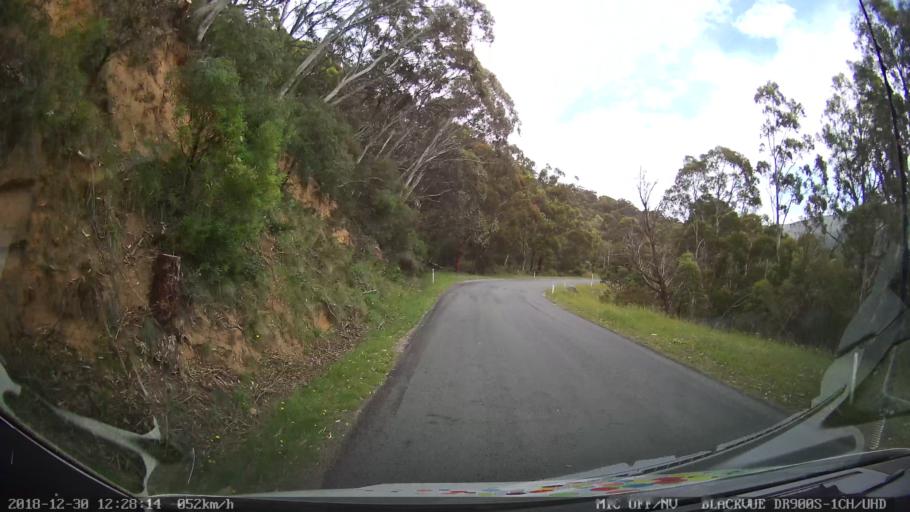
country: AU
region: New South Wales
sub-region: Snowy River
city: Jindabyne
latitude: -36.3264
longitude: 148.4866
